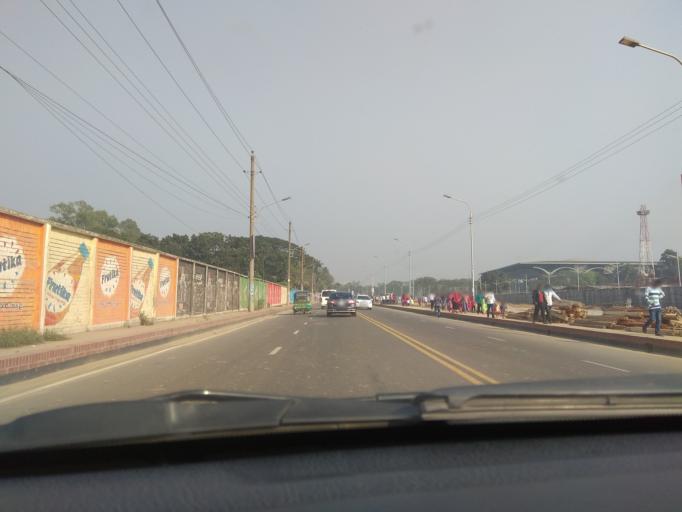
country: BD
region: Dhaka
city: Azimpur
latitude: 23.7702
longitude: 90.3779
